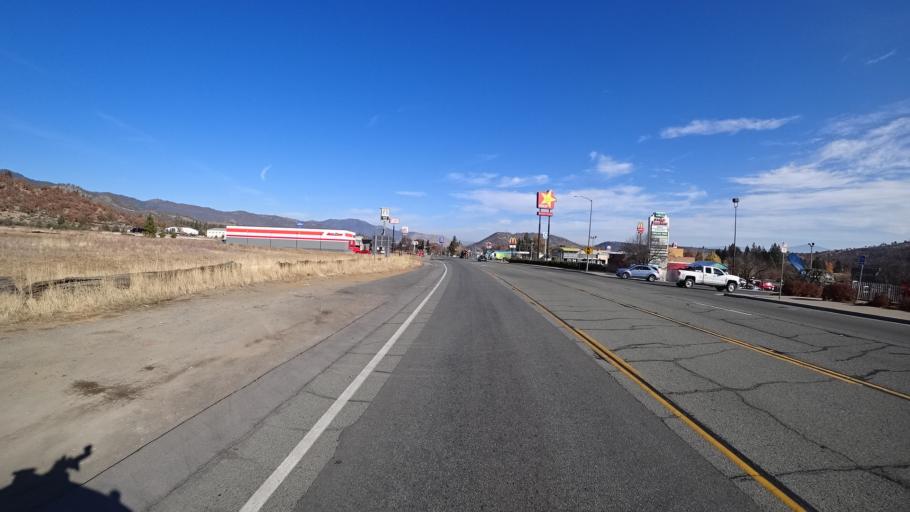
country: US
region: California
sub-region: Siskiyou County
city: Yreka
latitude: 41.7016
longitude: -122.6460
